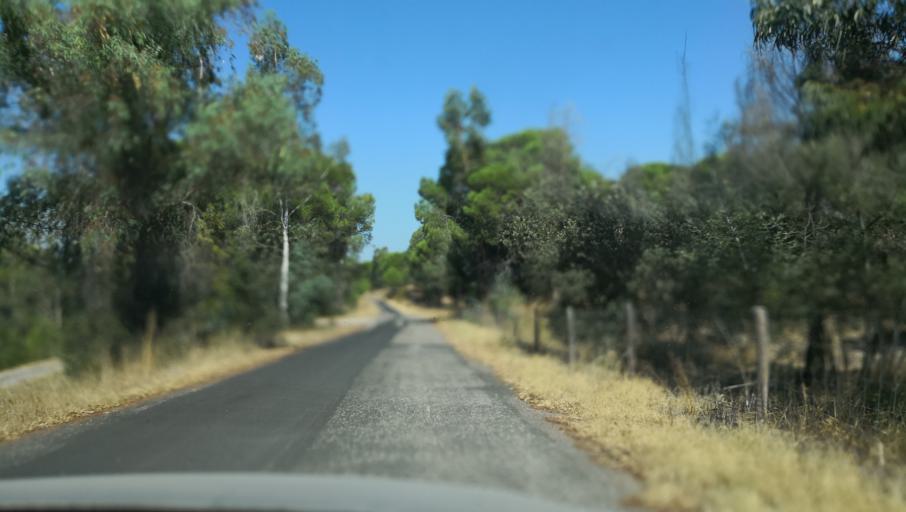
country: PT
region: Setubal
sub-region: Alcacer do Sal
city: Alcacer do Sal
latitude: 38.2508
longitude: -8.2975
